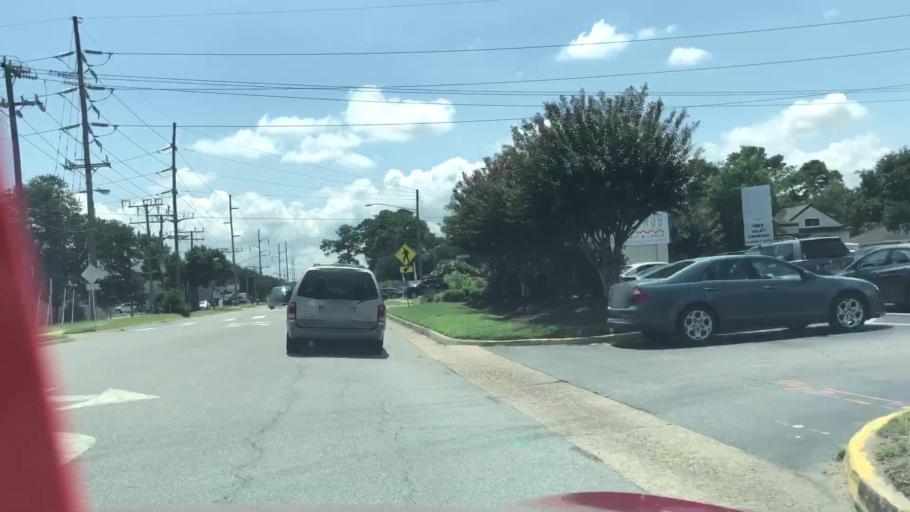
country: US
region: Virginia
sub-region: City of Virginia Beach
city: Virginia Beach
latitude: 36.9108
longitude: -76.0711
